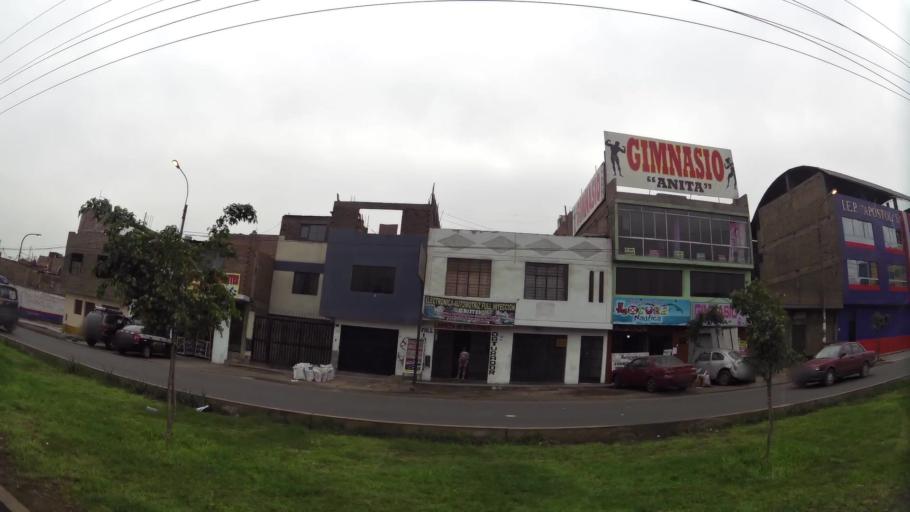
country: PE
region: Lima
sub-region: Lima
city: Independencia
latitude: -11.9626
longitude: -76.9852
